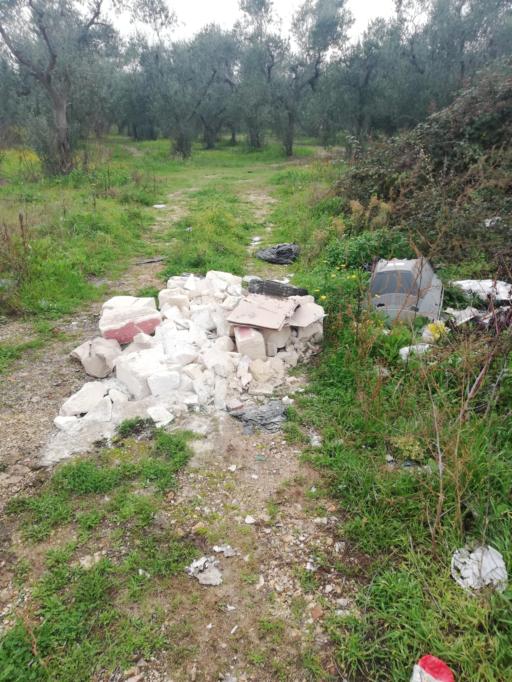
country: IT
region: Apulia
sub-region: Provincia di Bari
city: Palo del Colle
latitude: 41.0650
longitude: 16.6719
